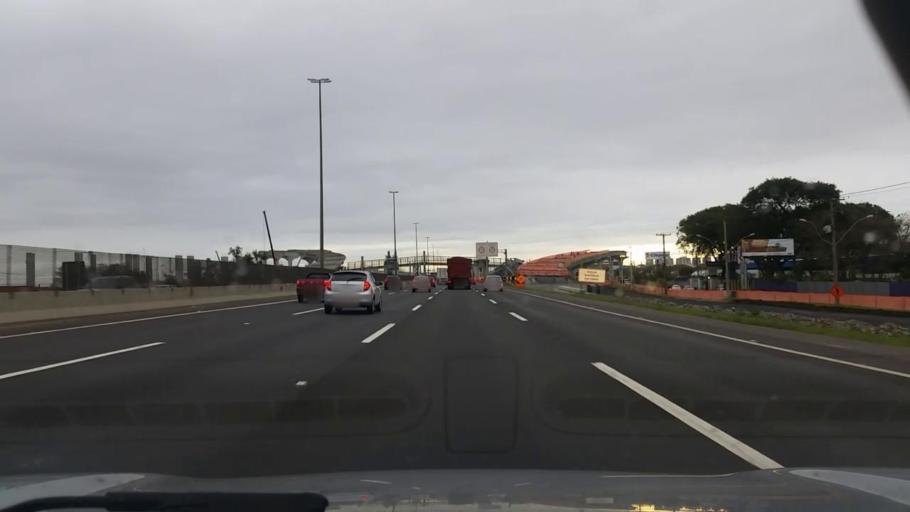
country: BR
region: Rio Grande do Sul
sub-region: Porto Alegre
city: Porto Alegre
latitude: -29.9923
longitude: -51.2046
